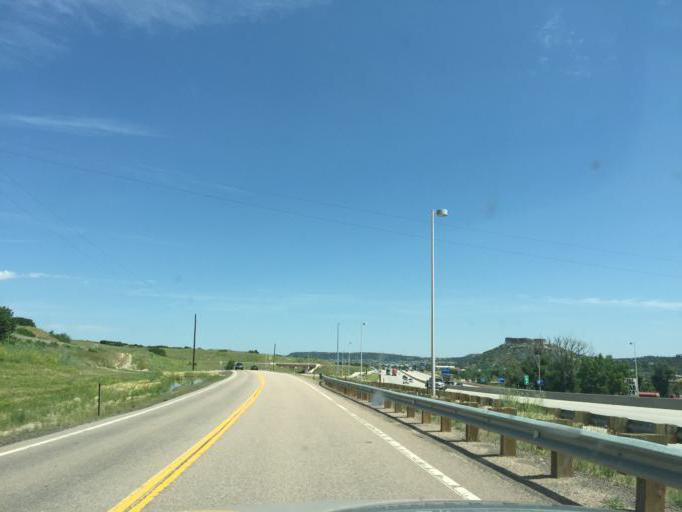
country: US
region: Colorado
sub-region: Douglas County
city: Castle Rock
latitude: 39.3617
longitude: -104.8673
